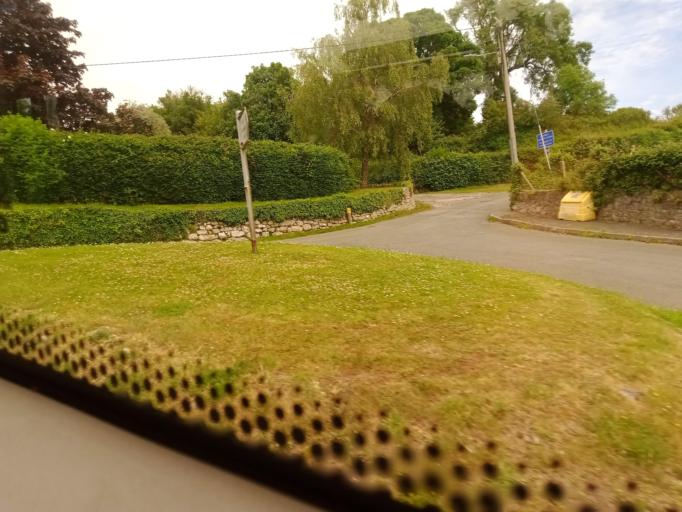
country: GB
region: Wales
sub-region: Anglesey
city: Llangoed
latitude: 53.2987
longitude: -4.0725
